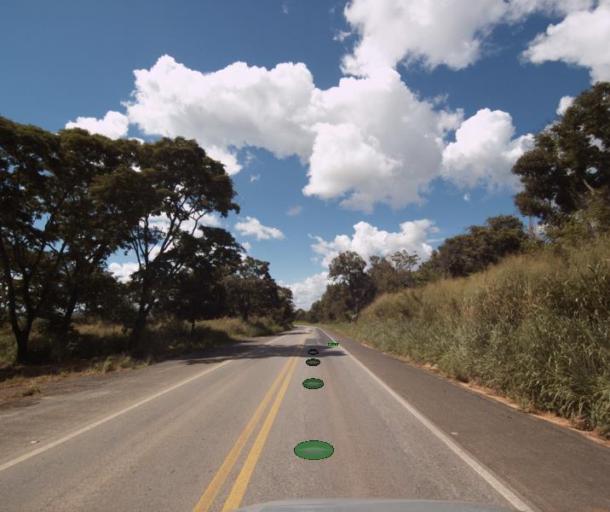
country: BR
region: Goias
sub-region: Porangatu
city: Porangatu
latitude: -13.7287
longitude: -49.0232
